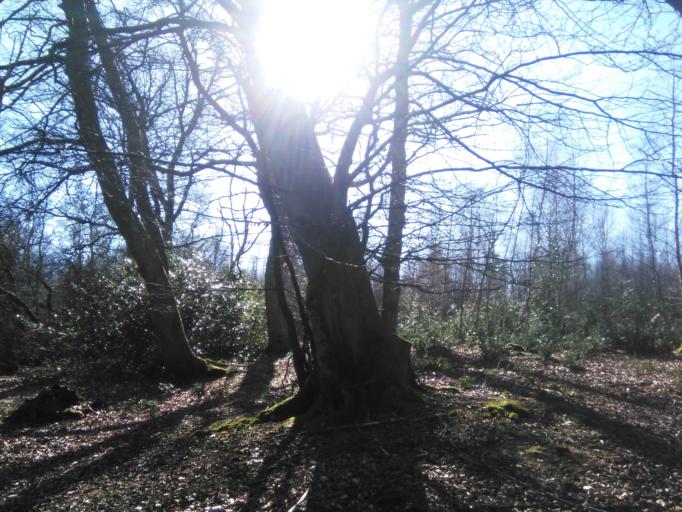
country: DK
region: Central Jutland
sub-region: Skanderborg Kommune
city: Ry
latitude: 56.1106
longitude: 9.7186
